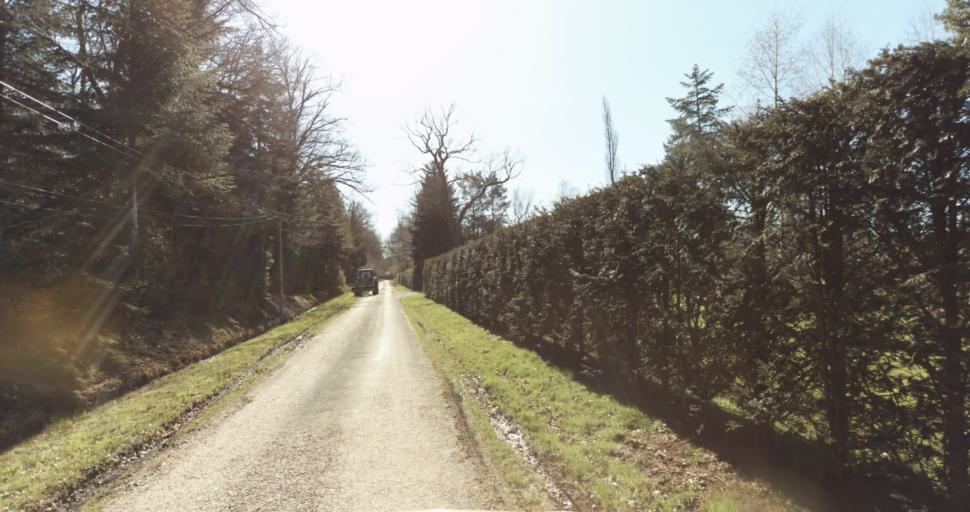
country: FR
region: Lower Normandy
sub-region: Departement du Calvados
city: Livarot
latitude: 48.9604
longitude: 0.0826
